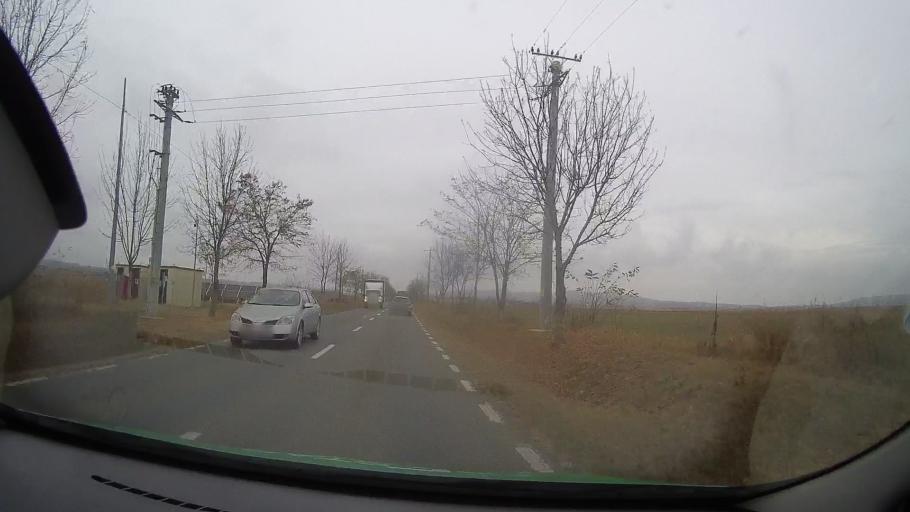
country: RO
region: Prahova
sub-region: Oras Baicoi
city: Liliesti
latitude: 45.0092
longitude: 25.8842
